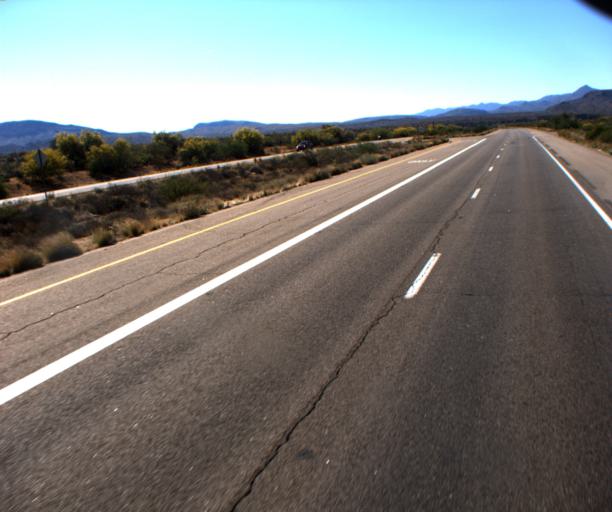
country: US
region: Arizona
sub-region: Yavapai County
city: Bagdad
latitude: 34.6541
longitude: -113.5745
